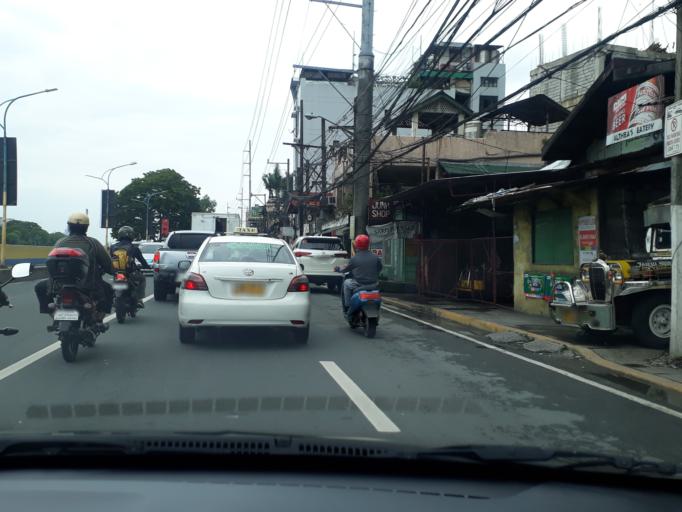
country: PH
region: Metro Manila
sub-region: Mandaluyong
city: Mandaluyong City
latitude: 14.5712
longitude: 121.0305
